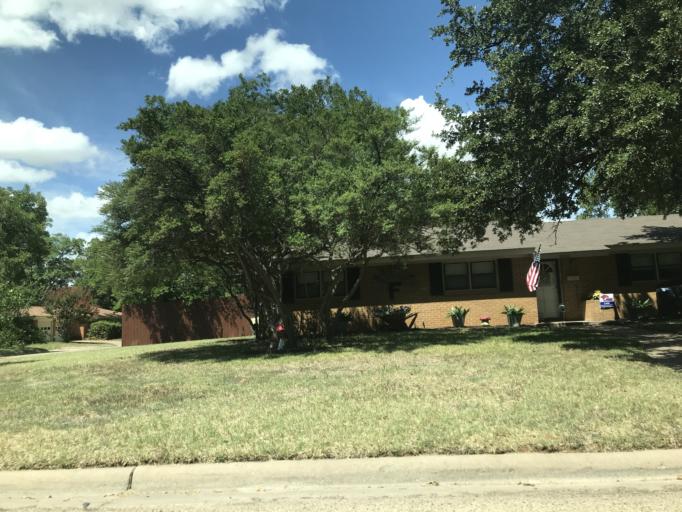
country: US
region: Texas
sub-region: Taylor County
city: Abilene
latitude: 32.4215
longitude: -99.7677
